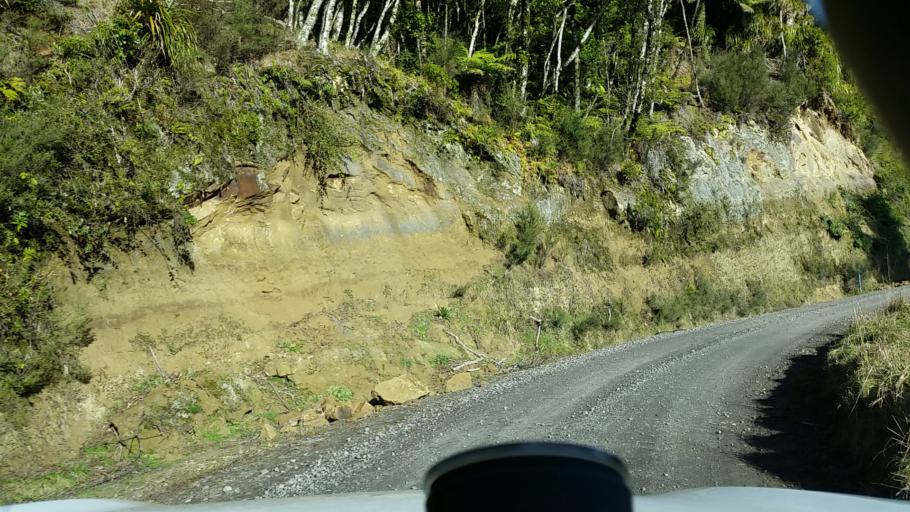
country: NZ
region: Taranaki
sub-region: South Taranaki District
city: Eltham
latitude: -39.4020
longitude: 174.5652
